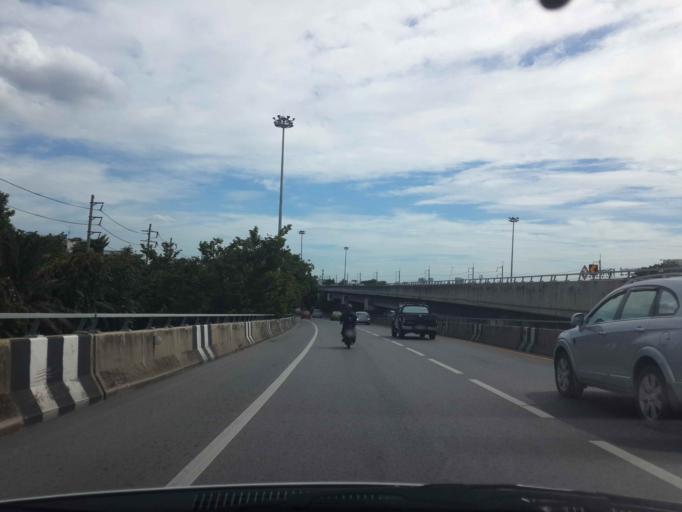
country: TH
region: Bangkok
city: Wang Thonglang
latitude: 13.7855
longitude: 100.6086
